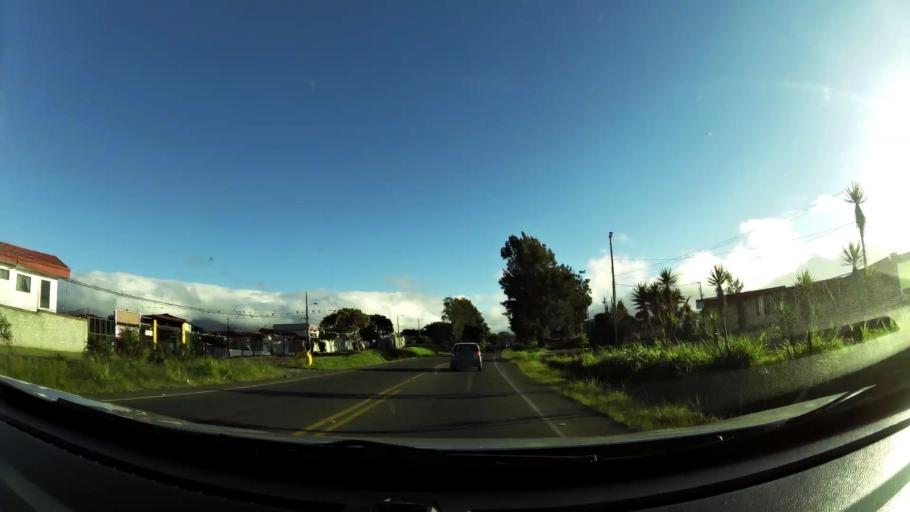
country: CR
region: Heredia
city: Angeles
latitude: 9.9881
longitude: -84.0438
